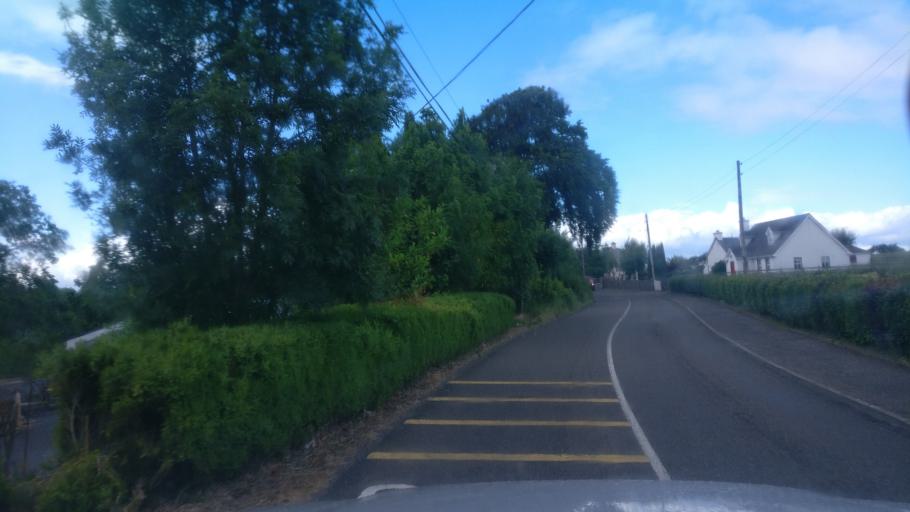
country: IE
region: Connaught
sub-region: County Galway
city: Portumna
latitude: 53.1692
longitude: -8.2916
